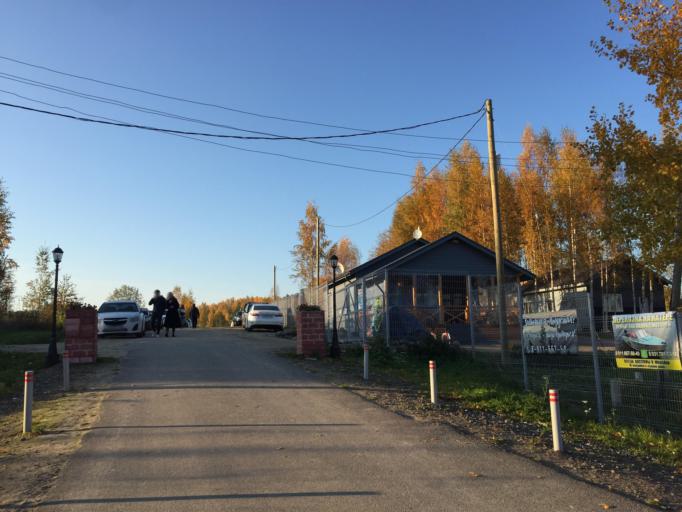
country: RU
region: Leningrad
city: Priozersk
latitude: 61.2865
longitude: 30.0891
